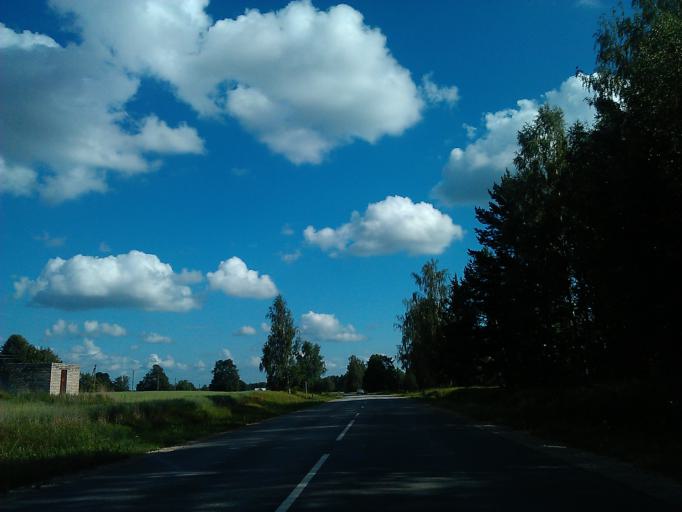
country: LV
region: Naukseni
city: Naukseni
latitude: 57.8318
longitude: 25.3893
